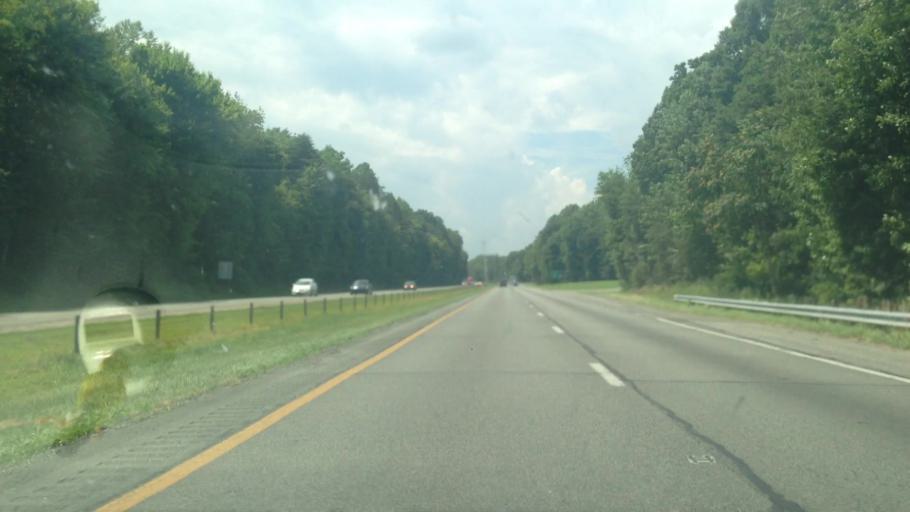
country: US
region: North Carolina
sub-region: Surry County
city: Pilot Mountain
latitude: 36.3364
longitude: -80.4556
